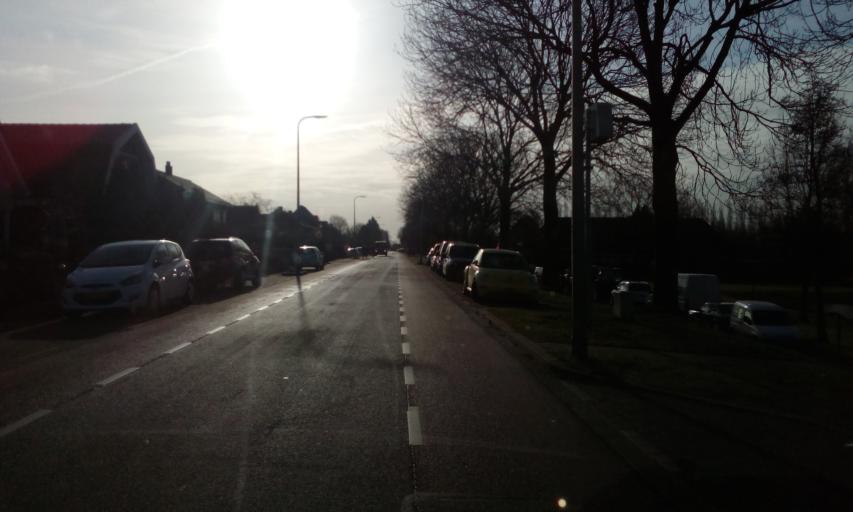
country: NL
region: South Holland
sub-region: Gemeente Zwijndrecht
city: Heerjansdam
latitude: 51.8591
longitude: 4.5668
